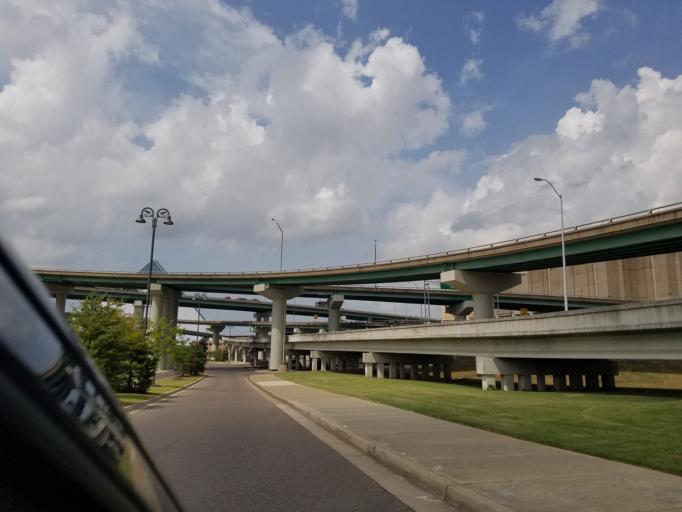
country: US
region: Tennessee
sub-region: Shelby County
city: Memphis
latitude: 35.1513
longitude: -90.0535
